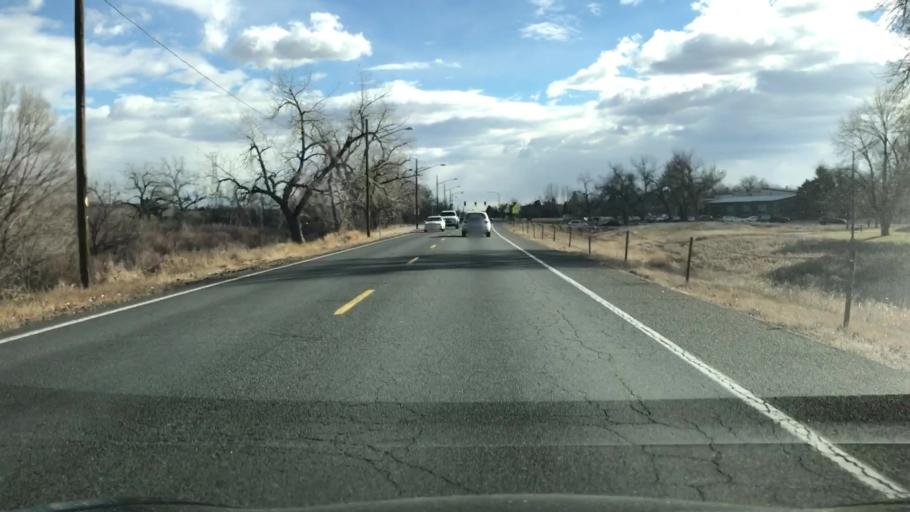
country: US
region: Colorado
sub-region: Arapahoe County
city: Glendale
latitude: 39.6892
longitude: -104.9106
